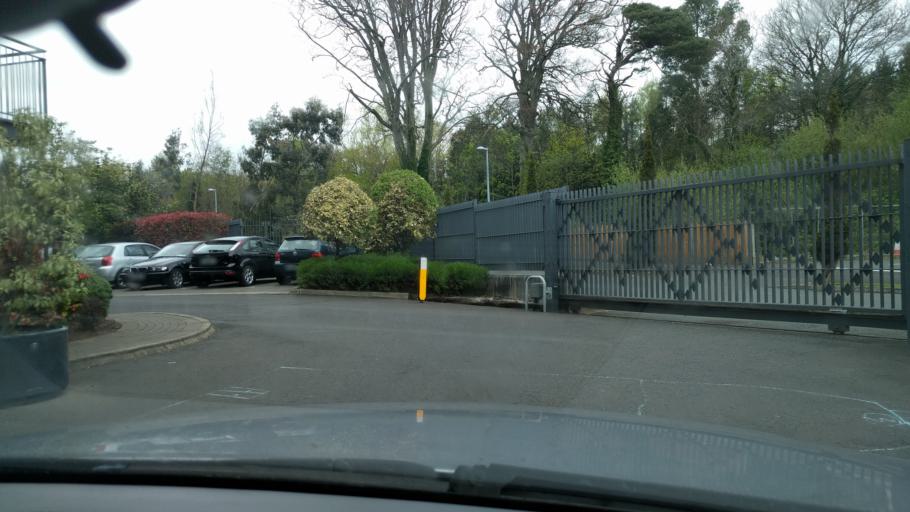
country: IE
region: Leinster
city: Little Bray
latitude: 53.1957
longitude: -6.1319
